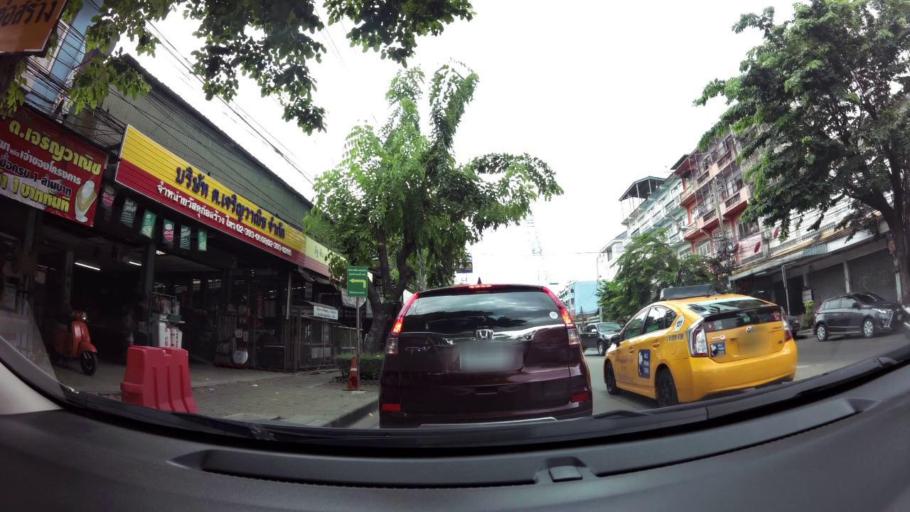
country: TH
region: Bangkok
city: Bang Na
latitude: 13.6779
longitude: 100.6366
